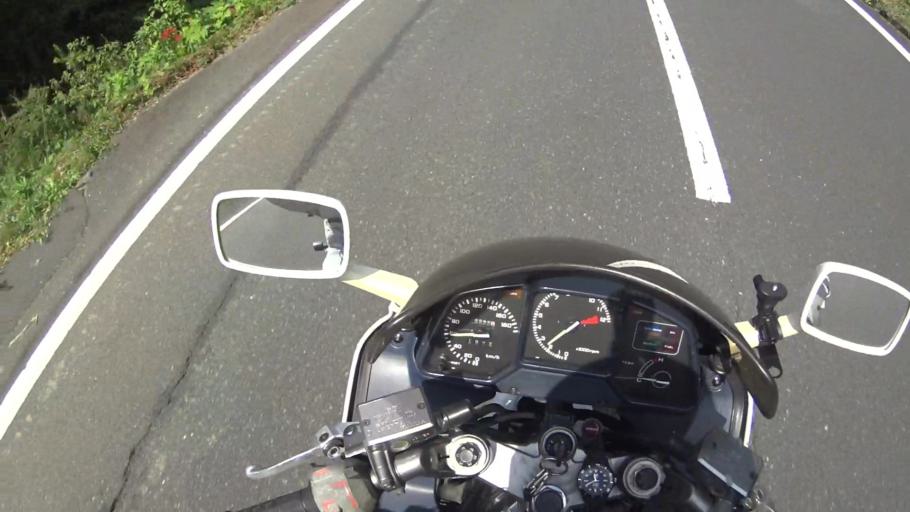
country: JP
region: Kyoto
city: Miyazu
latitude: 35.6928
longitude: 135.2508
